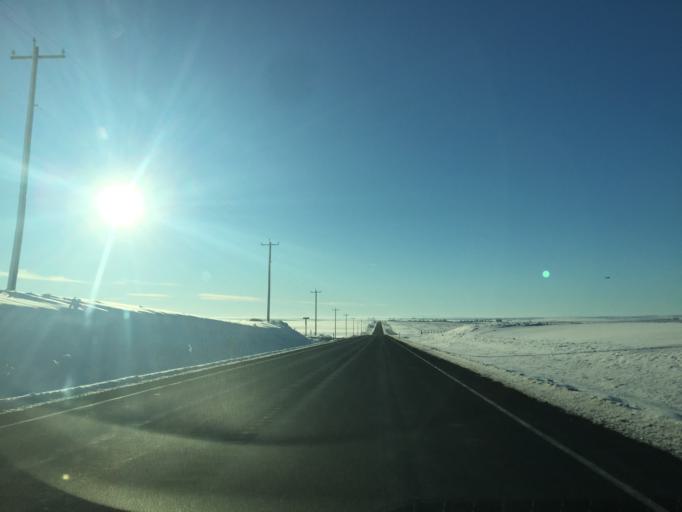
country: US
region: Washington
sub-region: Okanogan County
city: Coulee Dam
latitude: 47.7292
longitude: -118.8723
